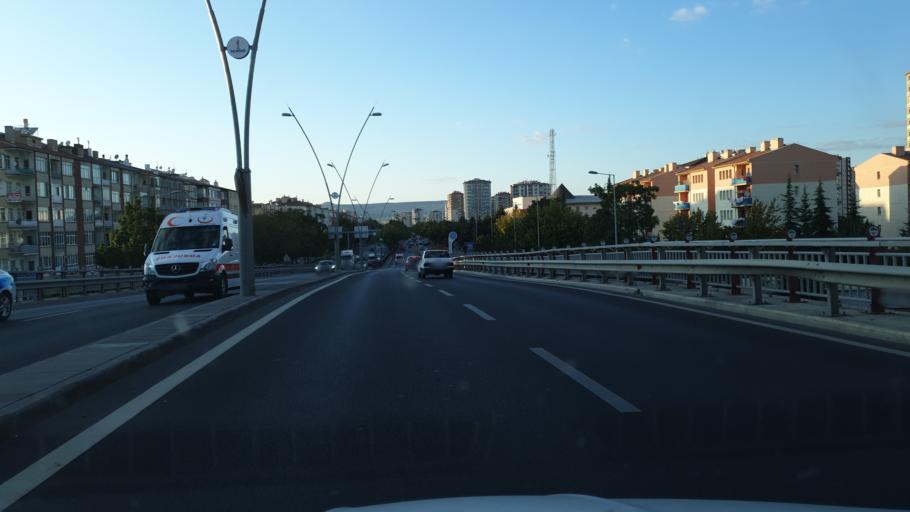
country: TR
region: Kayseri
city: Kayseri
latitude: 38.7361
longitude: 35.4929
